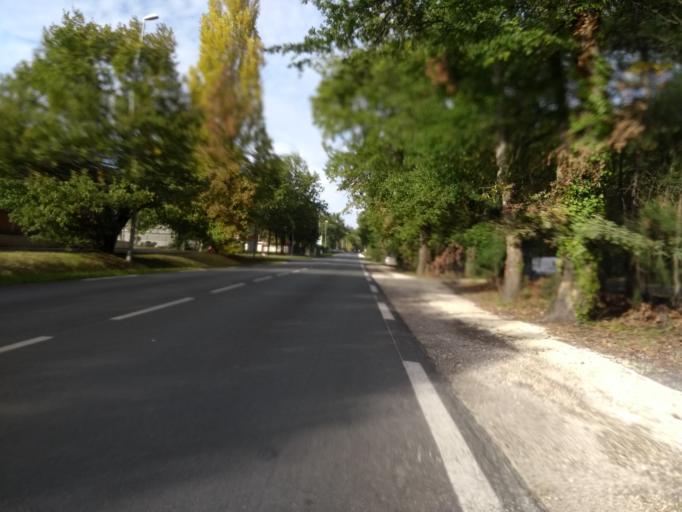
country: FR
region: Aquitaine
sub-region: Departement de la Gironde
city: Canejan
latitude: 44.7794
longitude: -0.6630
